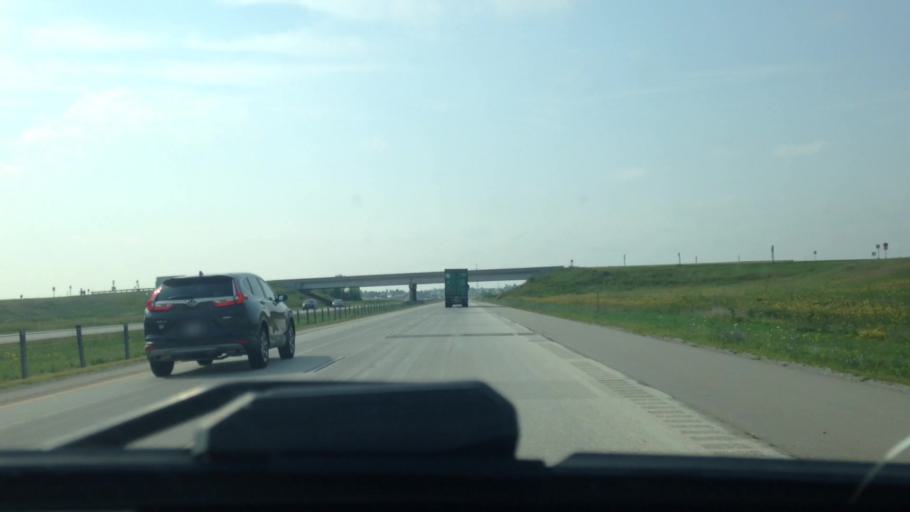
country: US
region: Wisconsin
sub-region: Dodge County
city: Lomira
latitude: 43.6184
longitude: -88.4387
